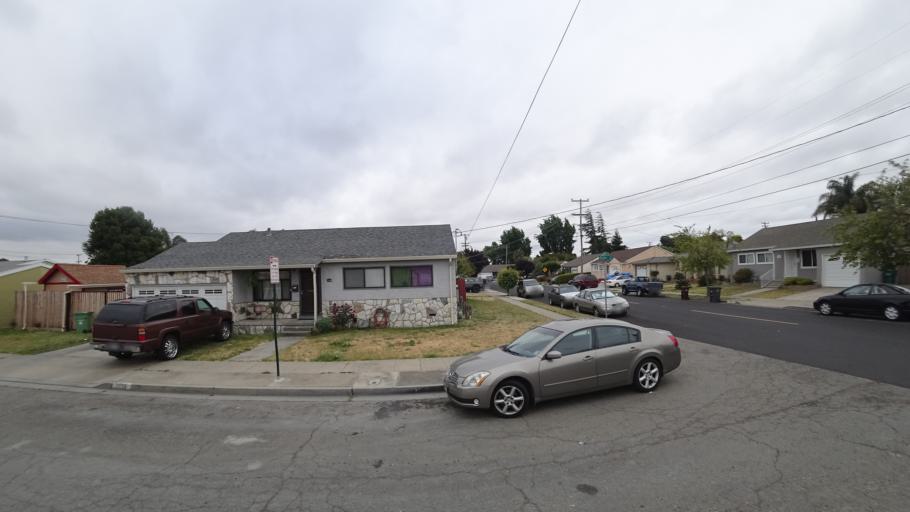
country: US
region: California
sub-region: Alameda County
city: Hayward
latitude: 37.6380
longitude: -122.0825
